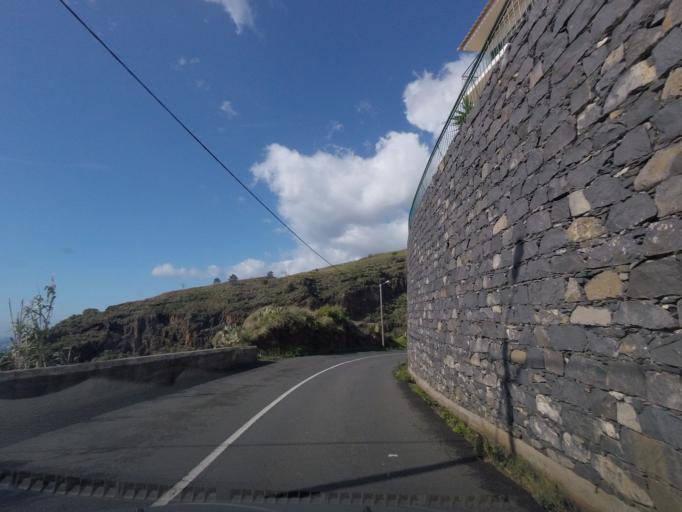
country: PT
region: Madeira
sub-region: Calheta
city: Estreito da Calheta
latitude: 32.7330
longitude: -17.1983
